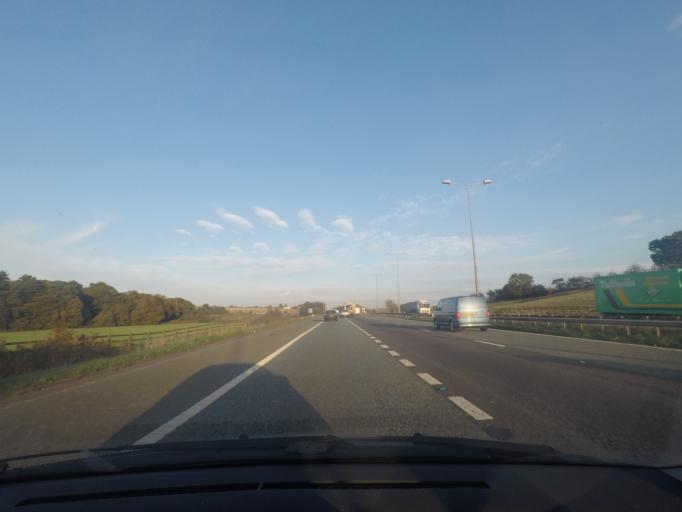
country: GB
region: England
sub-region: North Lincolnshire
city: Barnetby le Wold
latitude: 53.5835
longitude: -0.4267
